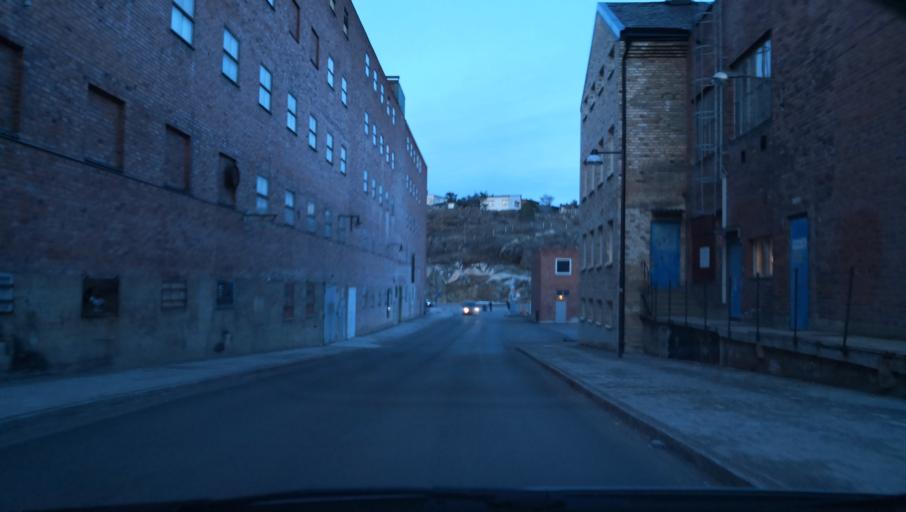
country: SE
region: Stockholm
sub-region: Varmdo Kommun
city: Gustavsberg
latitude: 59.3231
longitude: 18.3839
